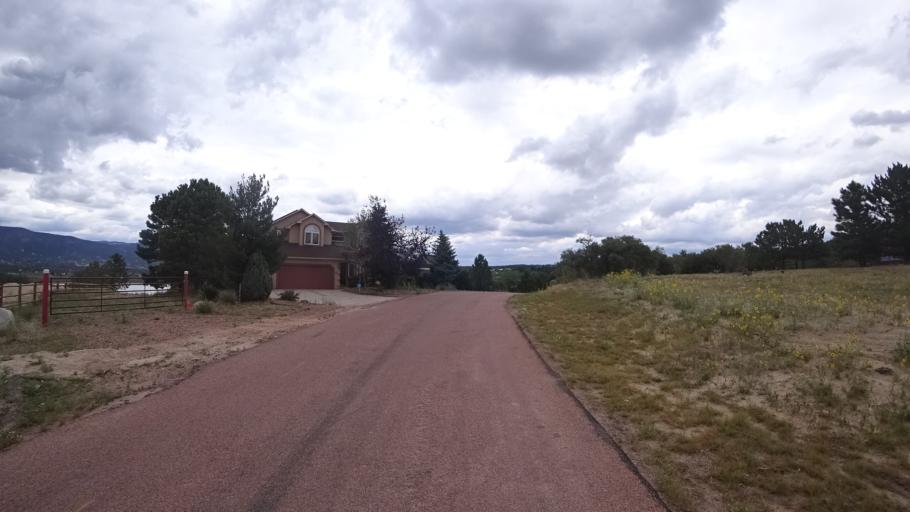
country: US
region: Colorado
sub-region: El Paso County
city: Woodmoor
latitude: 39.0985
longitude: -104.8536
